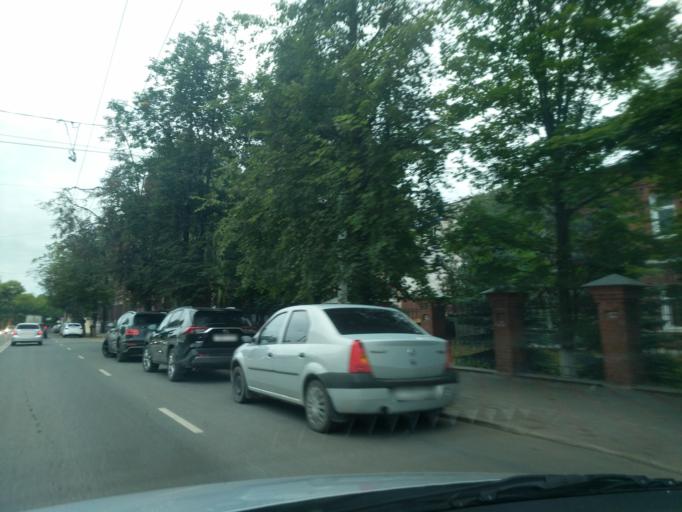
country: RU
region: Kirov
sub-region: Kirovo-Chepetskiy Rayon
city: Kirov
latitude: 58.6133
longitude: 49.6671
